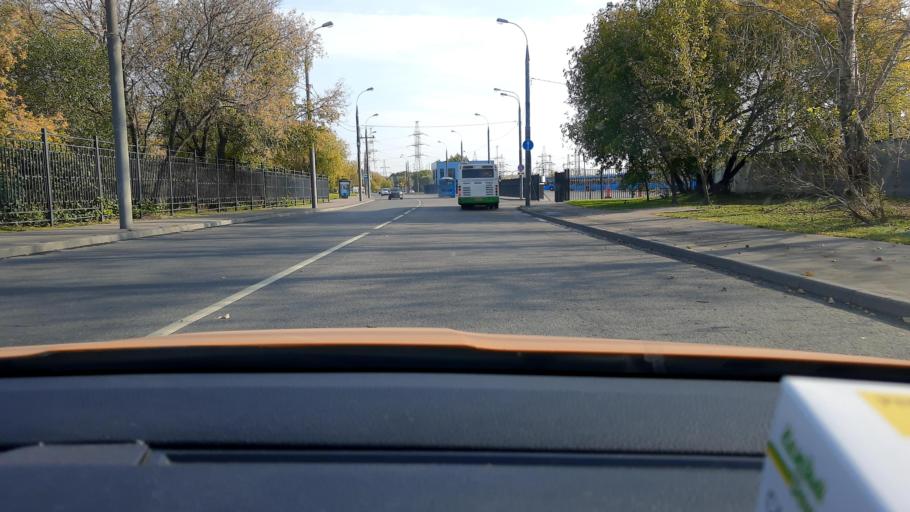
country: RU
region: Moscow
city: Kuz'minki
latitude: 55.6763
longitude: 37.7952
